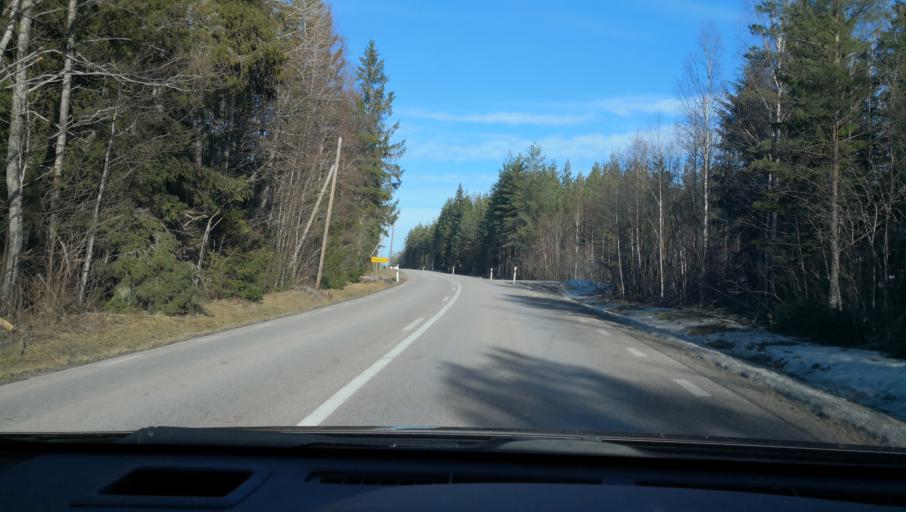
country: SE
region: Uppsala
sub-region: Osthammars Kommun
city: Osterbybruk
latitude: 60.1466
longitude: 17.8263
